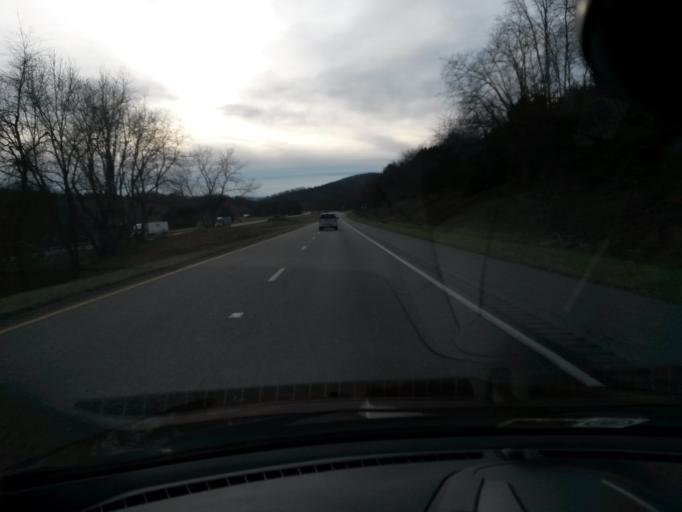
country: US
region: Virginia
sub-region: City of Lexington
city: Lexington
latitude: 37.8585
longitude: -79.4852
